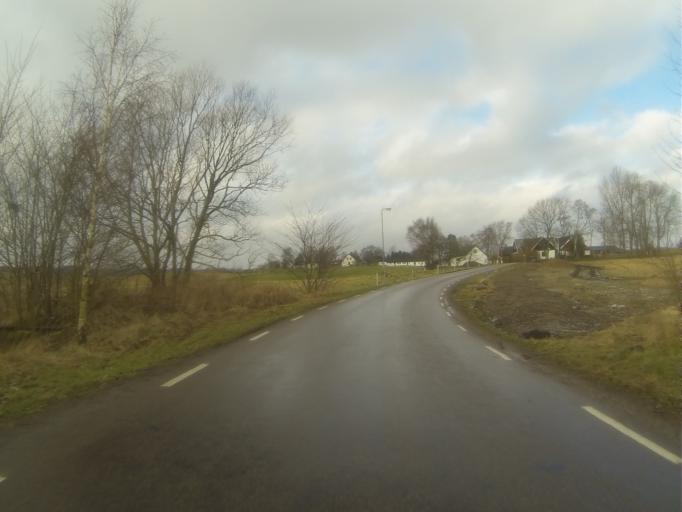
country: SE
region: Skane
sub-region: Svedala Kommun
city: Klagerup
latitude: 55.5702
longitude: 13.3047
